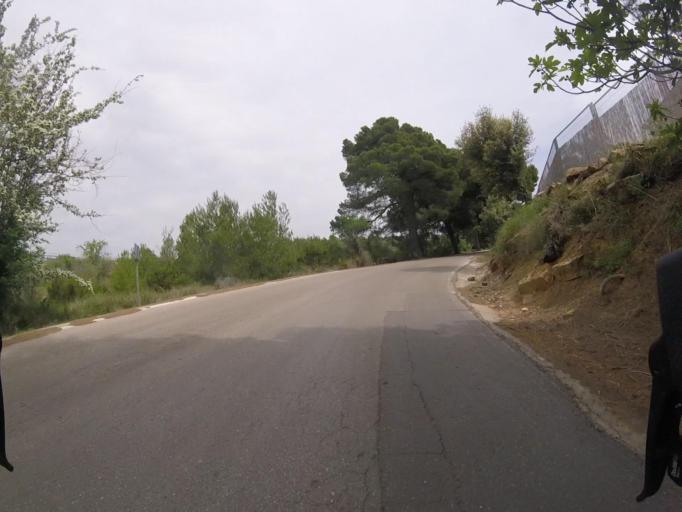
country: ES
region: Valencia
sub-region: Provincia de Castello
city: Cabanes
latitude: 40.1540
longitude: 0.0532
